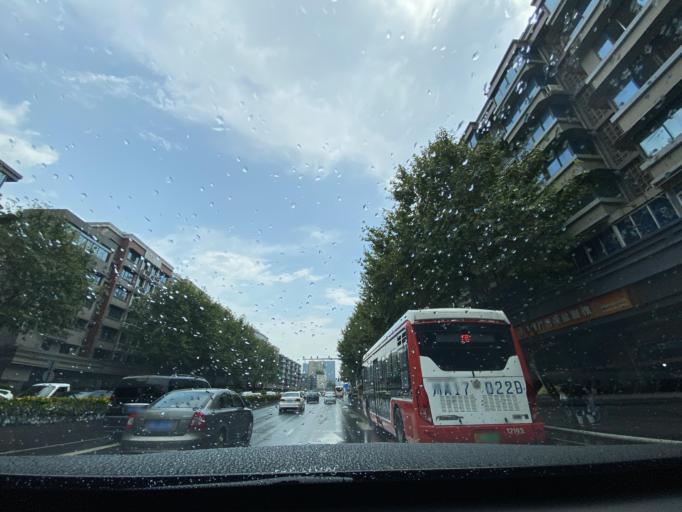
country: CN
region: Sichuan
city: Chengdu
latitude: 30.6427
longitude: 104.0732
